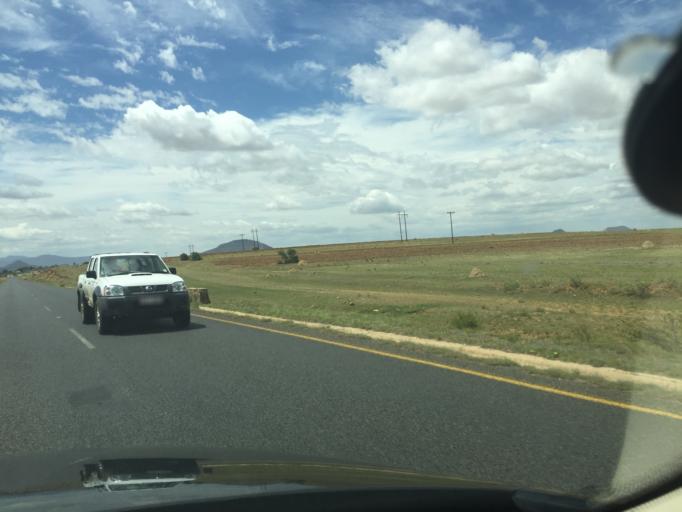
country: LS
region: Mohale's Hoek District
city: Mohale's Hoek
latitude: -30.0028
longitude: 27.3450
